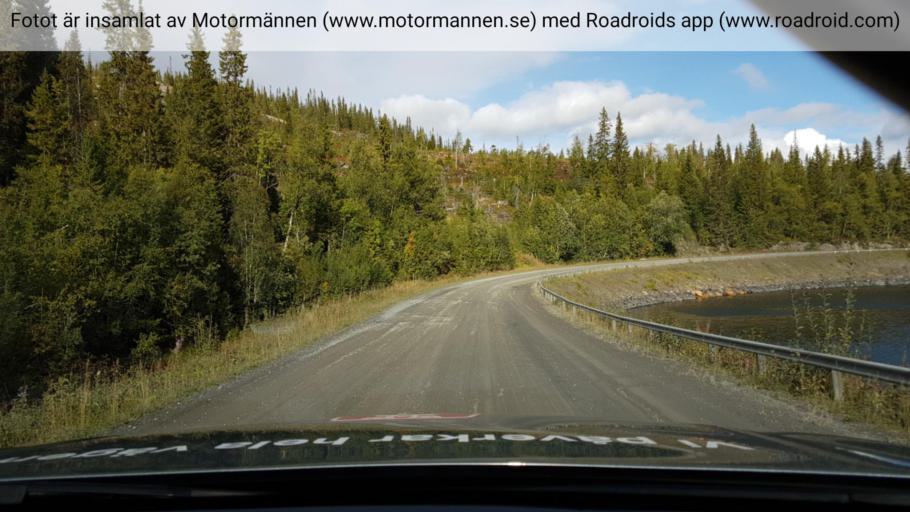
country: SE
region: Jaemtland
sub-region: Are Kommun
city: Are
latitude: 63.6974
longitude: 12.9373
